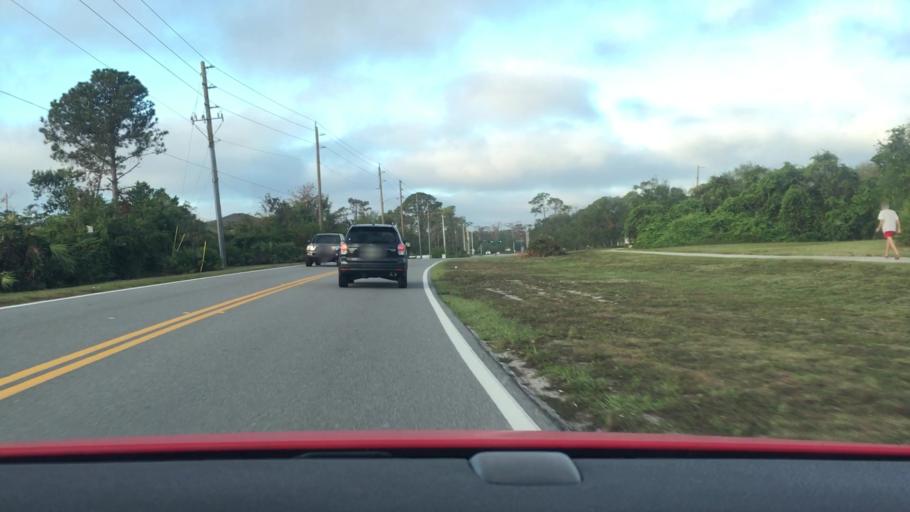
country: US
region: Florida
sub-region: Volusia County
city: South Daytona
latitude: 29.1577
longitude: -81.0346
